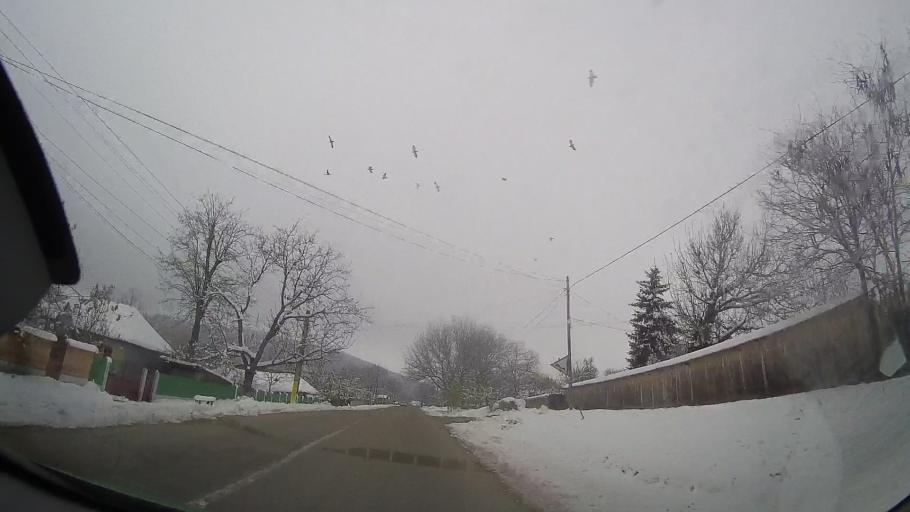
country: RO
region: Neamt
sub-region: Comuna Oniceni
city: Oniceni
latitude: 46.8002
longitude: 27.1496
